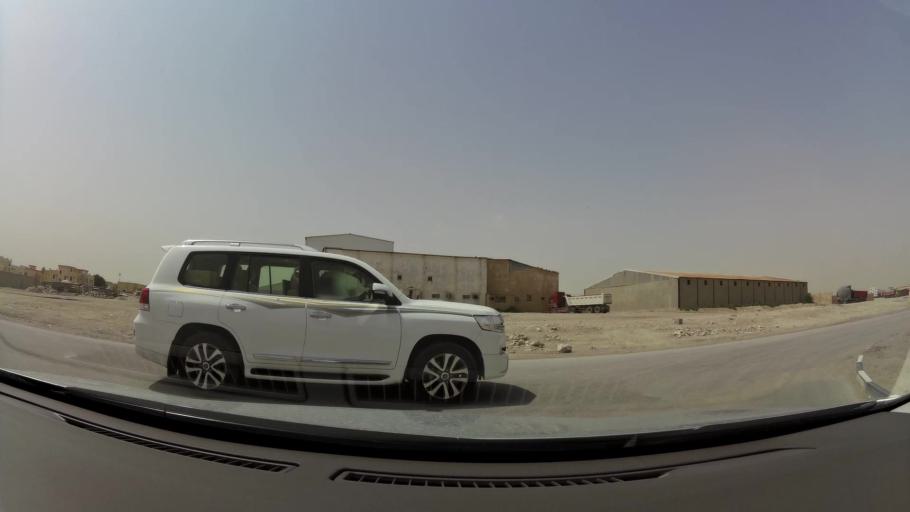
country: QA
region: Baladiyat ar Rayyan
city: Ar Rayyan
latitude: 25.2383
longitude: 51.4175
